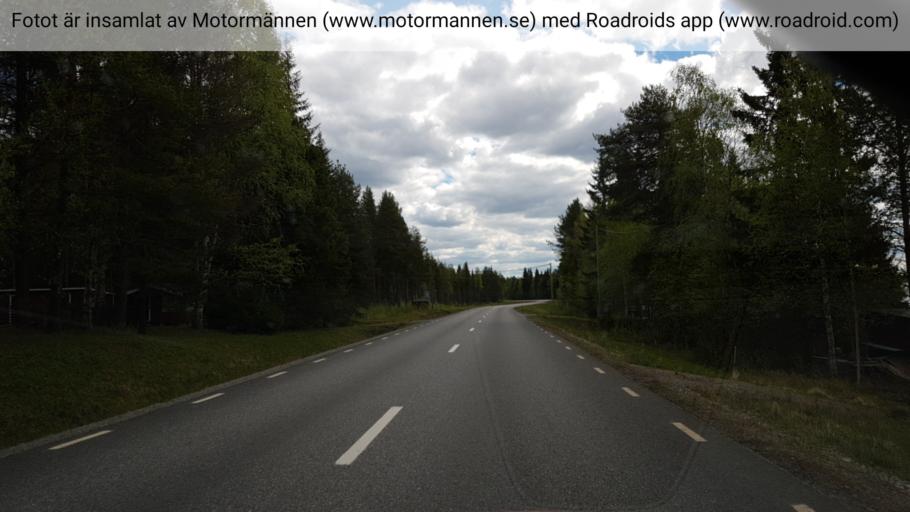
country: SE
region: Vaesterbotten
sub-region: Norsjo Kommun
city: Norsjoe
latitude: 64.8398
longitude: 19.7624
